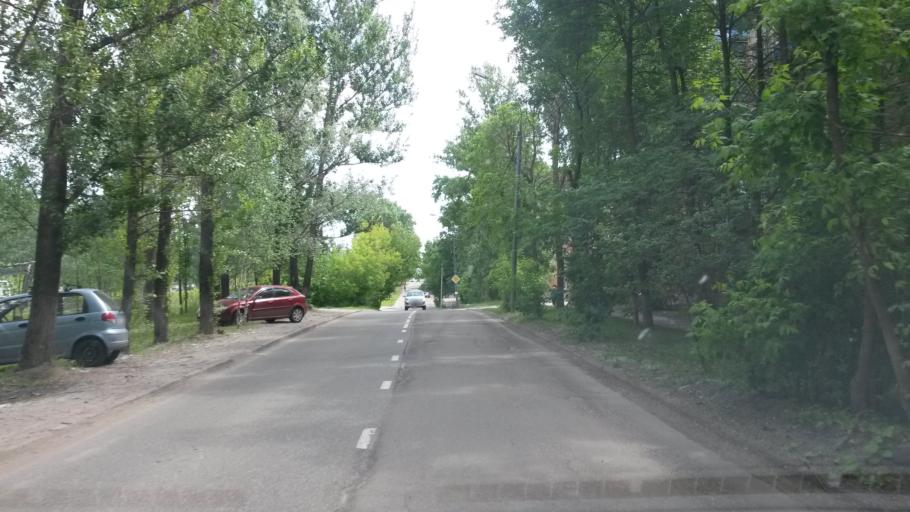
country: RU
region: Jaroslavl
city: Yaroslavl
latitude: 57.5876
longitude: 39.8367
